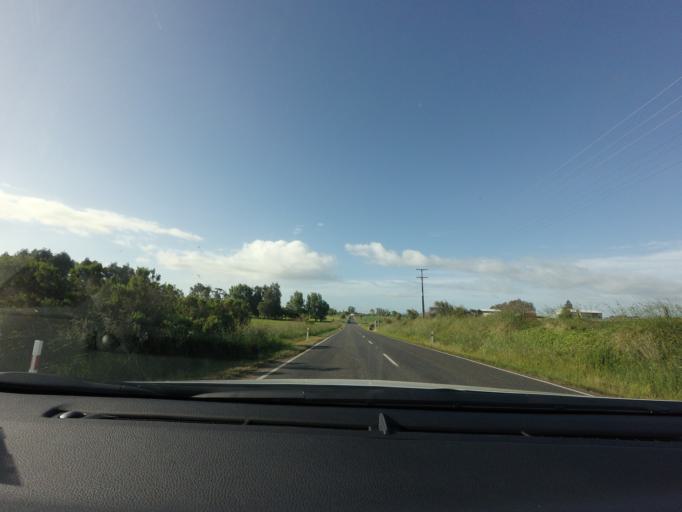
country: NZ
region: Waikato
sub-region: Hauraki District
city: Paeroa
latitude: -37.4737
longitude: 175.5092
